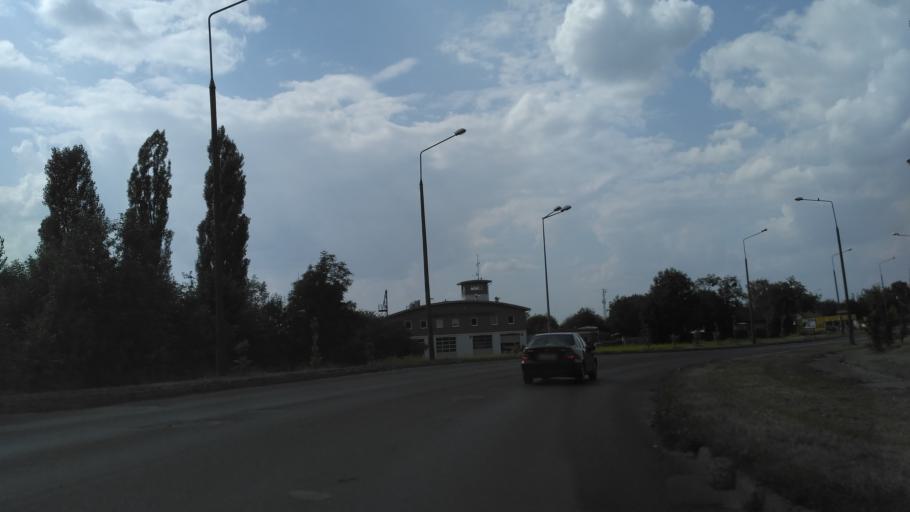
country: PL
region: Lublin Voivodeship
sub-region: Chelm
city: Chelm
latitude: 51.1424
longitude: 23.4851
